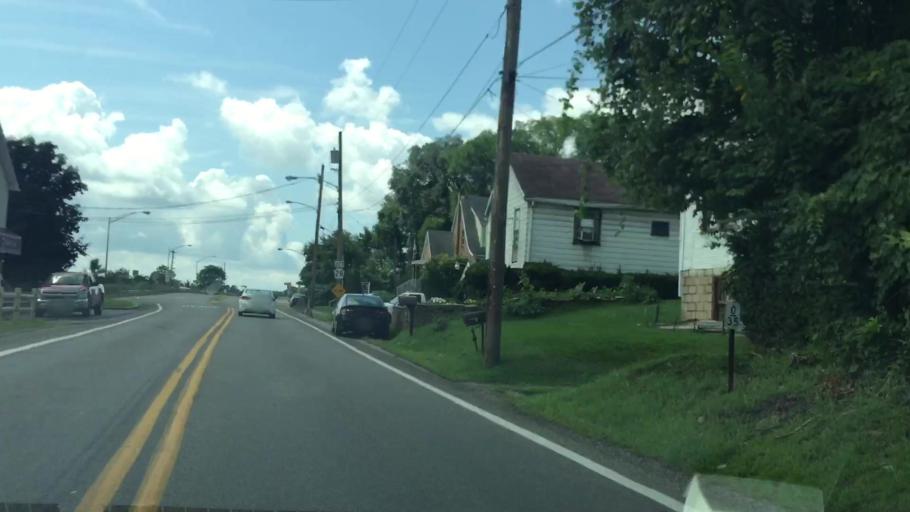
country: US
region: Pennsylvania
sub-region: Allegheny County
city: Cheswick
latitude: 40.5559
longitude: -79.8075
